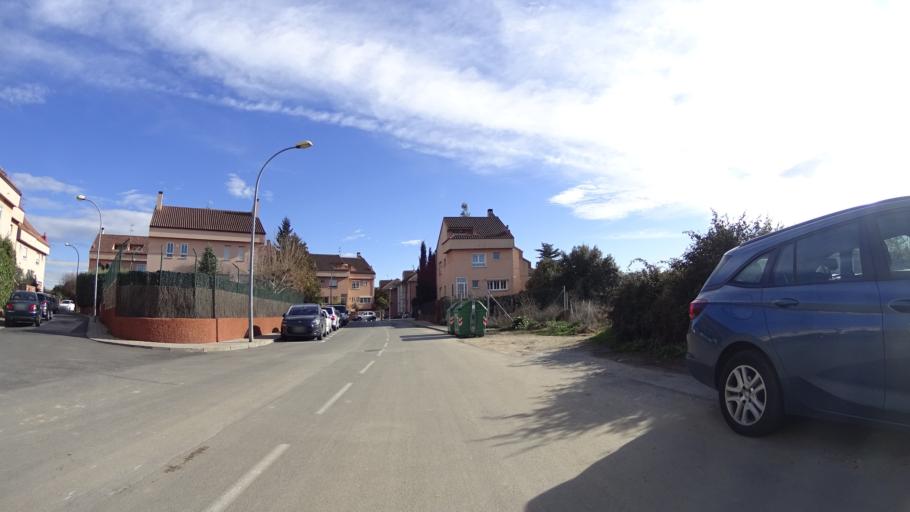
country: ES
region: Madrid
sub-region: Provincia de Madrid
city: Galapagar
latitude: 40.5807
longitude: -4.0152
